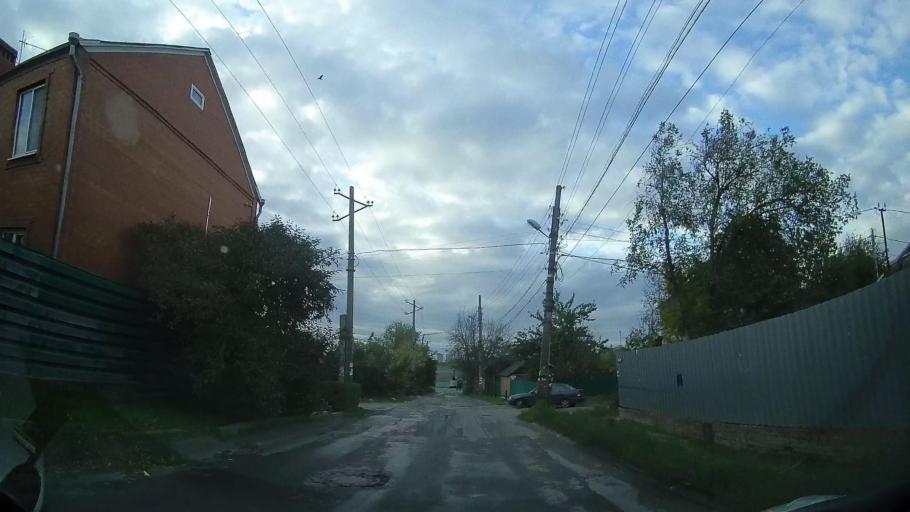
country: RU
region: Rostov
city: Severnyy
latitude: 47.2660
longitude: 39.6739
